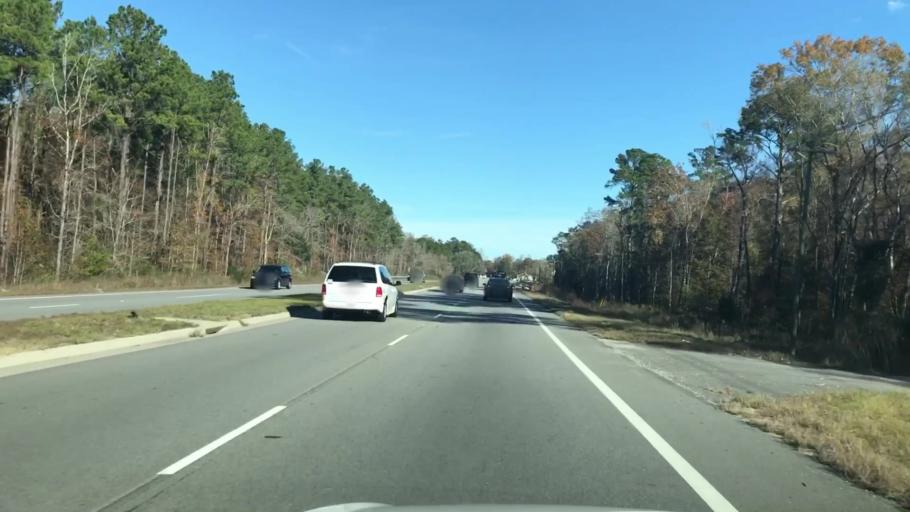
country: US
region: South Carolina
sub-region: Dorchester County
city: Centerville
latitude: 32.9534
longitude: -80.2017
